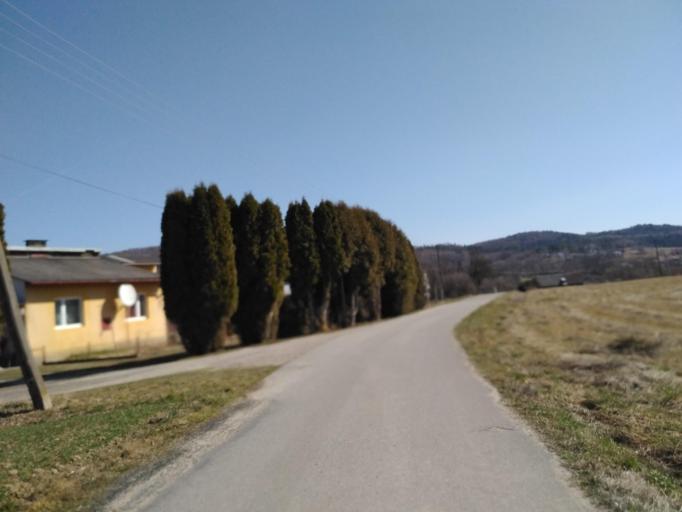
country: PL
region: Subcarpathian Voivodeship
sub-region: Powiat brzozowski
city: Jasienica Rosielna
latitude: 49.7625
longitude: 21.9550
